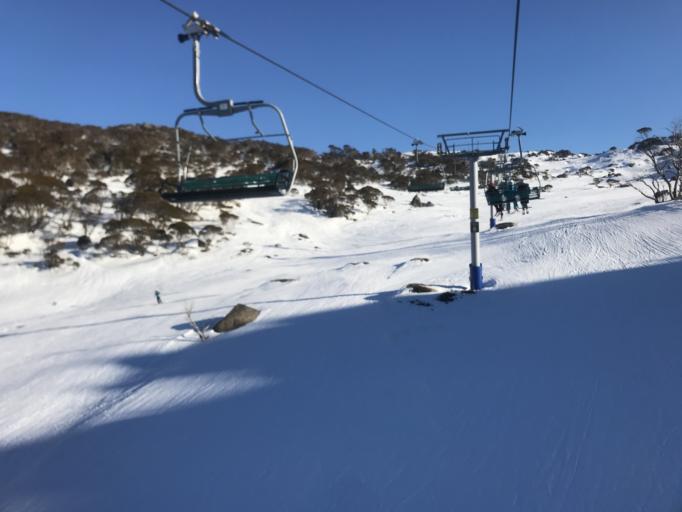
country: AU
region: New South Wales
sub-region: Snowy River
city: Jindabyne
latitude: -36.3895
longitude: 148.3970
